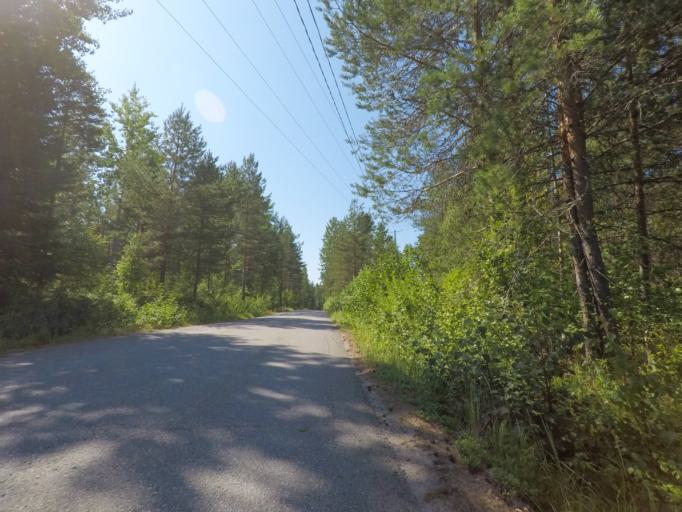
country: FI
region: Southern Savonia
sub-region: Mikkeli
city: Puumala
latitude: 61.4074
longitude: 28.0862
